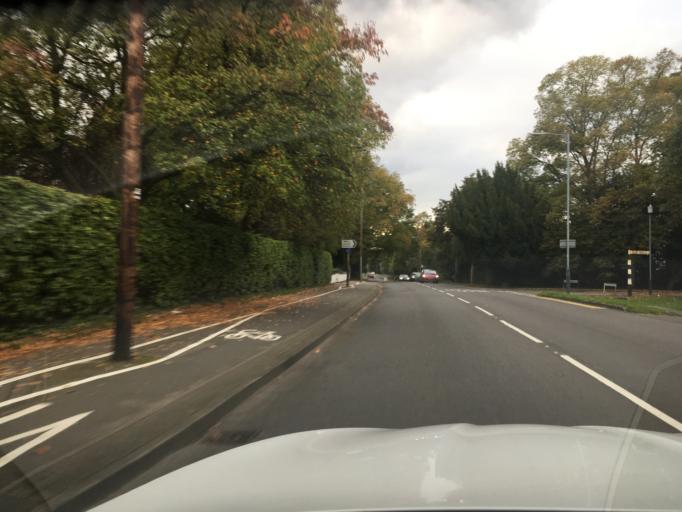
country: GB
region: England
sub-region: Warwickshire
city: Warwick
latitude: 52.2816
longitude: -1.5612
